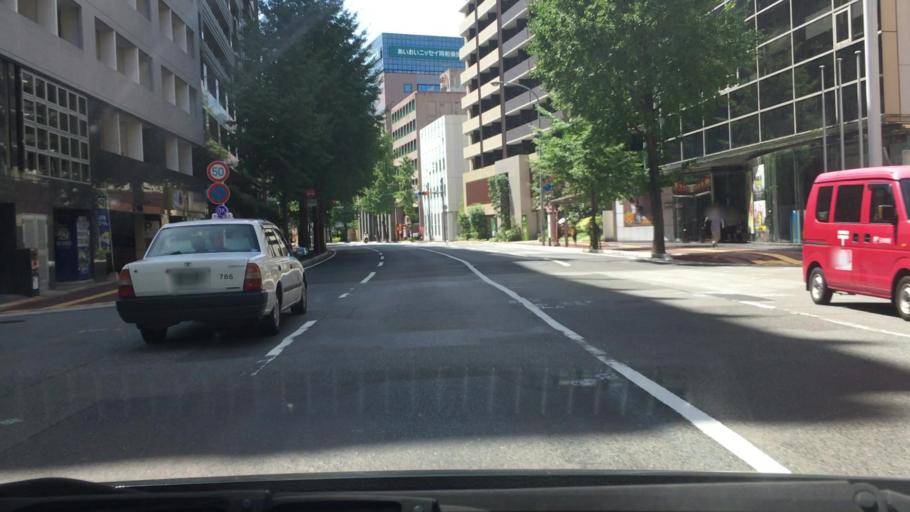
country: JP
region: Fukuoka
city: Fukuoka-shi
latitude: 33.5888
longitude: 130.4132
